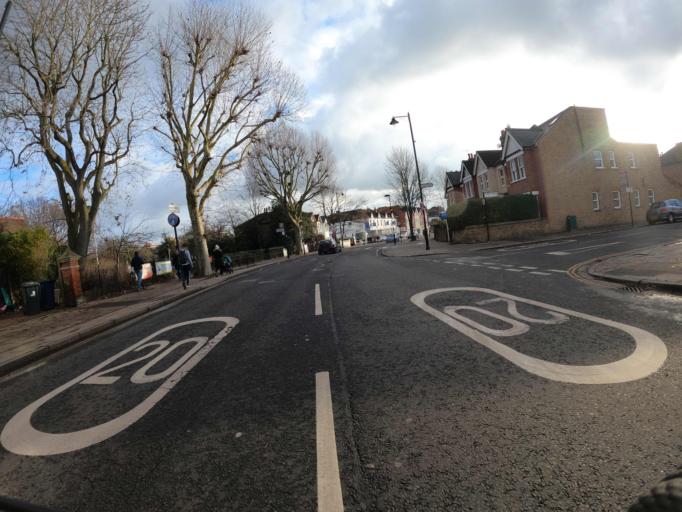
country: GB
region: England
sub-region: Greater London
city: Ealing
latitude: 51.5017
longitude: -0.3157
